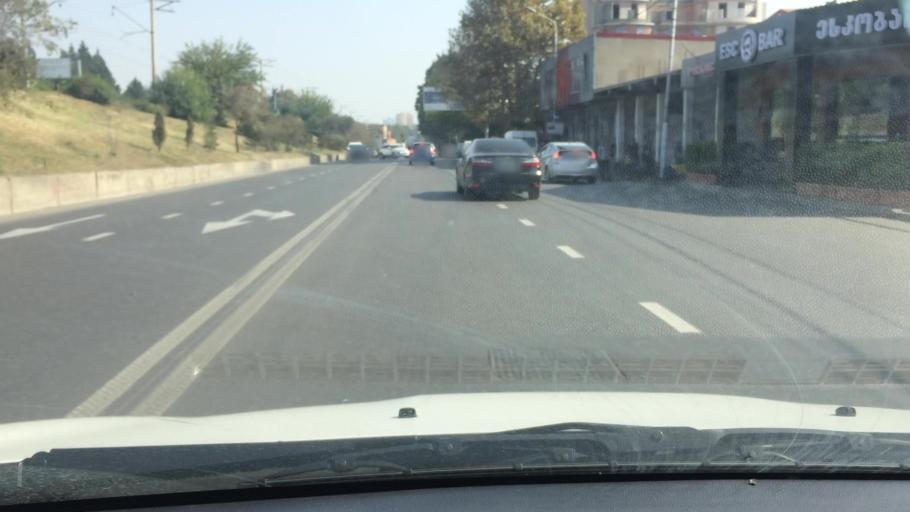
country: GE
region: T'bilisi
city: Tbilisi
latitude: 41.6914
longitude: 44.8314
